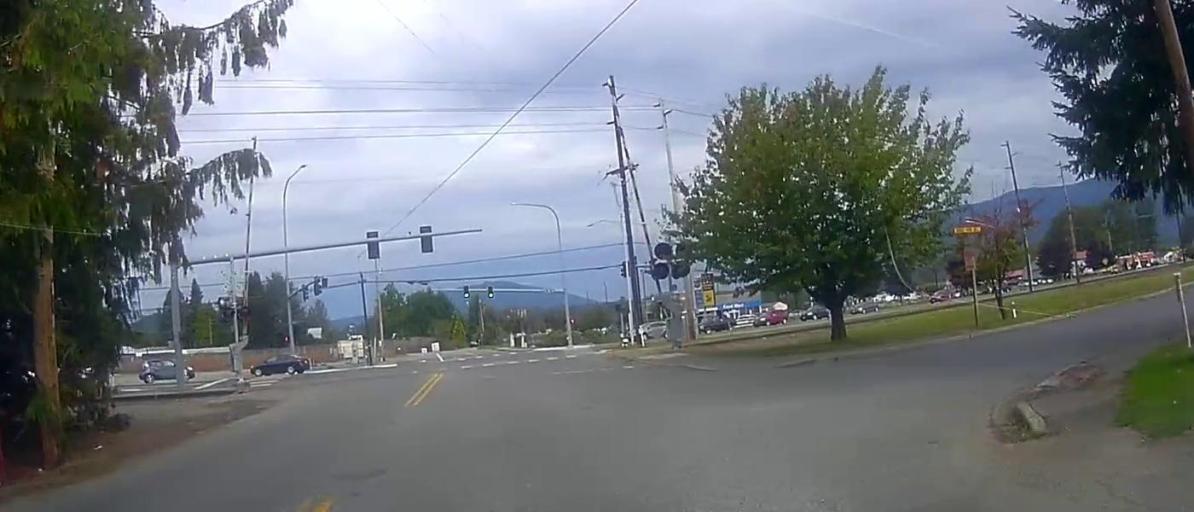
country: US
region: Washington
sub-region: Skagit County
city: Sedro-Woolley
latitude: 48.5000
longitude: -122.2584
